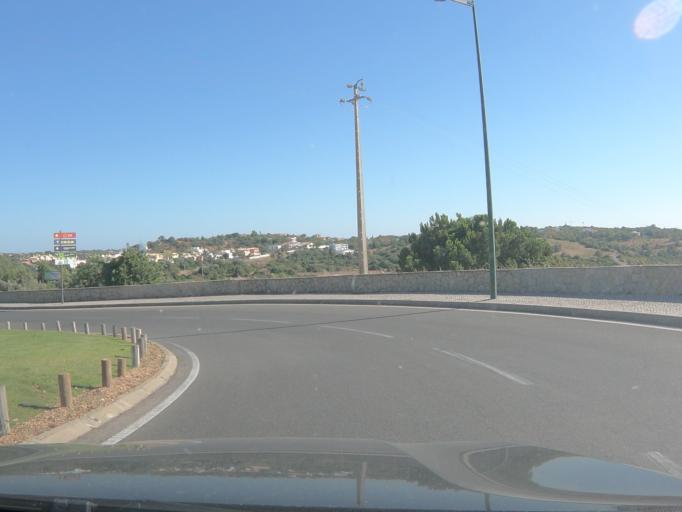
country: PT
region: Faro
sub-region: Loule
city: Loule
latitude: 37.1268
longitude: -8.0176
